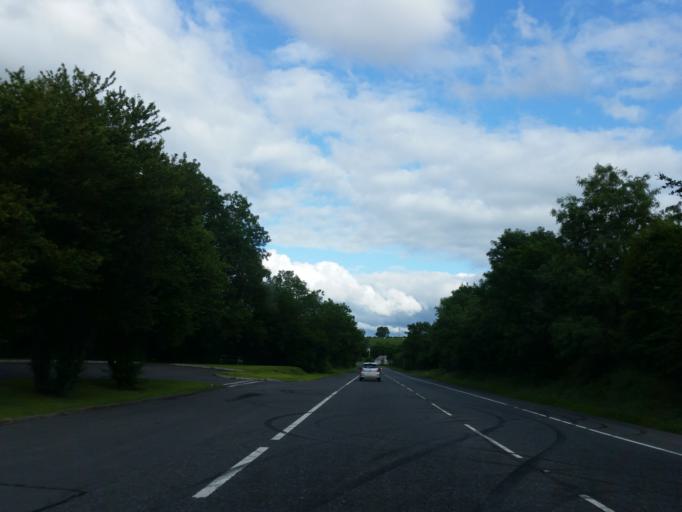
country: GB
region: Northern Ireland
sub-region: Fermanagh District
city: Enniskillen
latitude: 54.3184
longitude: -7.5865
